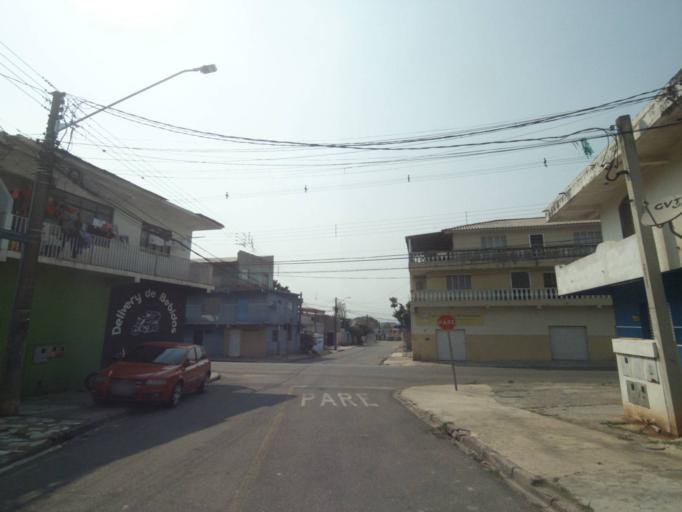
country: BR
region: Parana
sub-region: Pinhais
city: Pinhais
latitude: -25.4837
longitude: -49.2055
